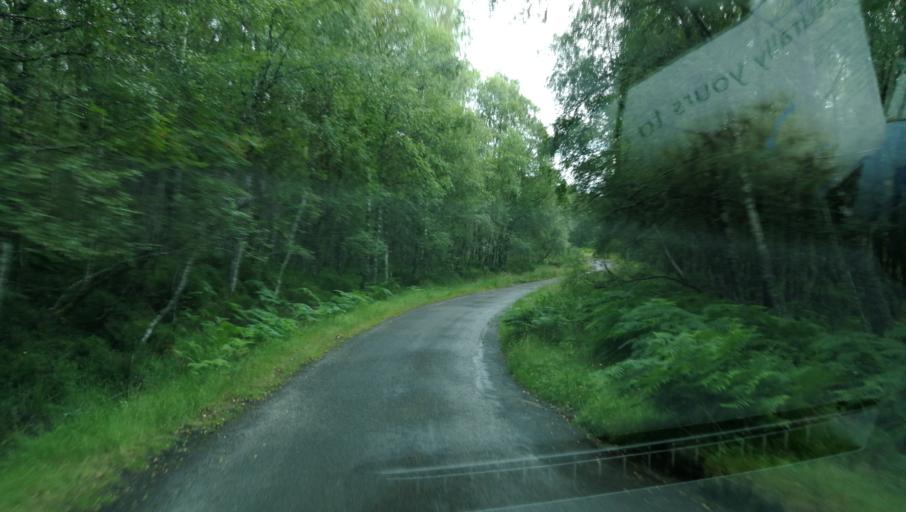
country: GB
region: Scotland
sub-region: Highland
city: Spean Bridge
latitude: 57.3106
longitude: -4.8640
